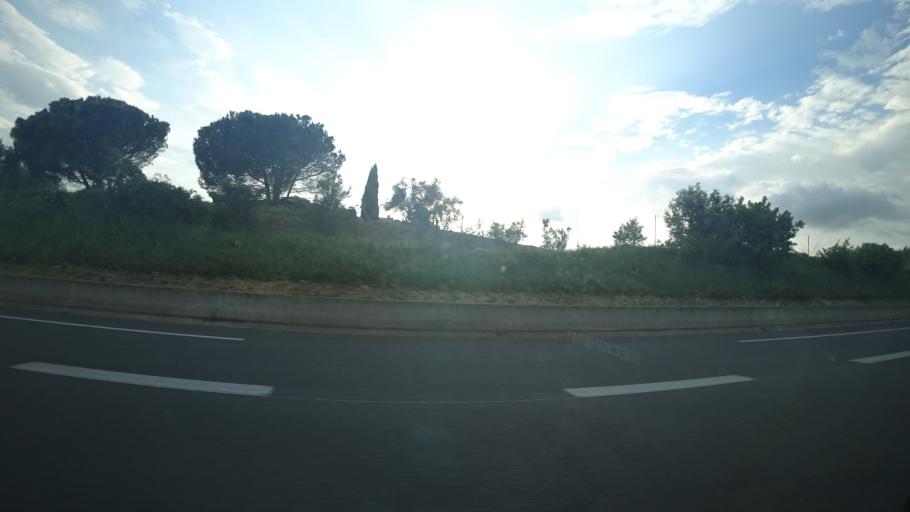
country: FR
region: Languedoc-Roussillon
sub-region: Departement de l'Herault
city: Nebian
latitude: 43.6483
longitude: 3.4498
